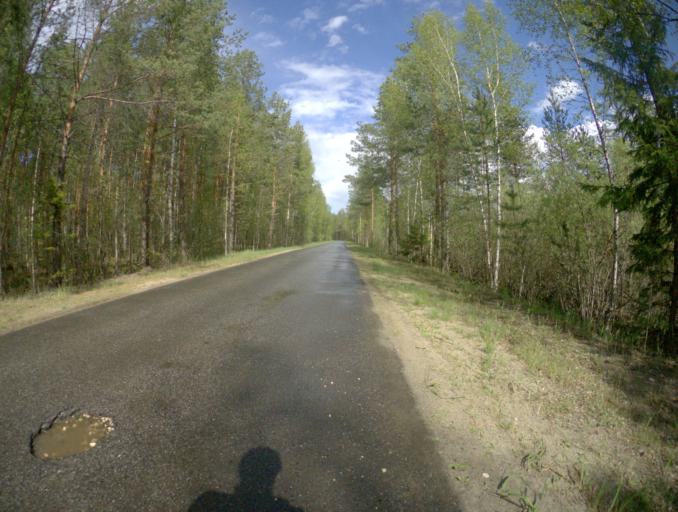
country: RU
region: Vladimir
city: Urshel'skiy
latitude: 55.5846
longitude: 40.2055
